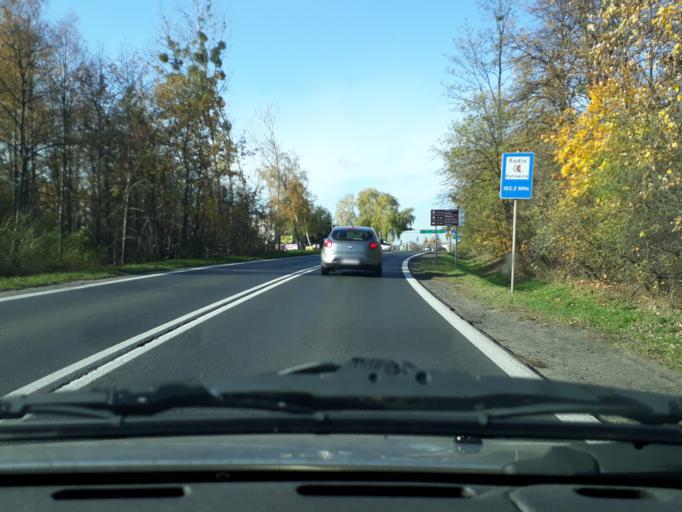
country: PL
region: Silesian Voivodeship
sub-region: Powiat tarnogorski
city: Tarnowskie Gory
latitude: 50.4310
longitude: 18.8704
